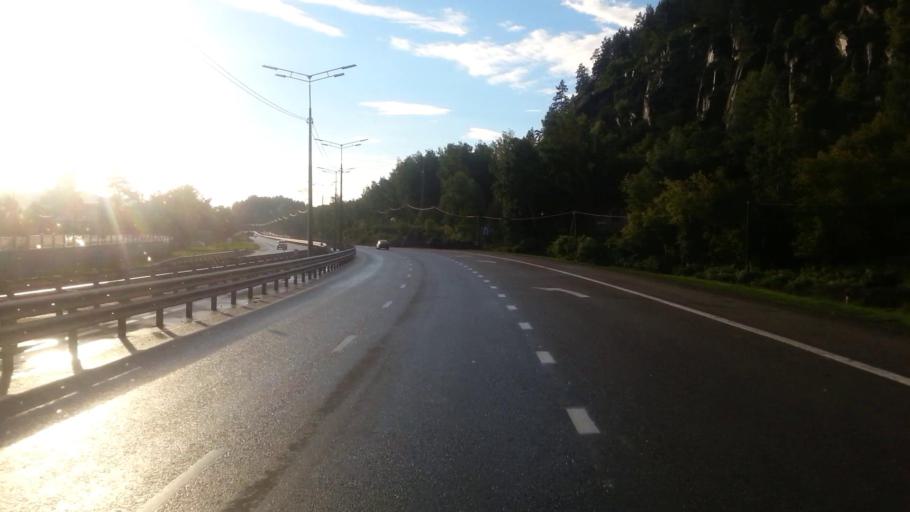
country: RU
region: Altay
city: Souzga
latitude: 51.9189
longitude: 85.8580
